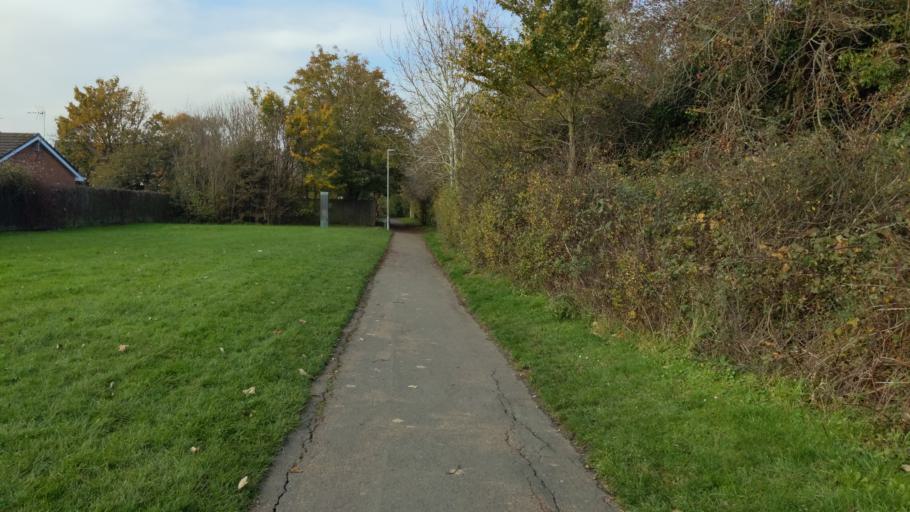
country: GB
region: England
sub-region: Buckinghamshire
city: Winslow
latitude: 51.9444
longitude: -0.8751
